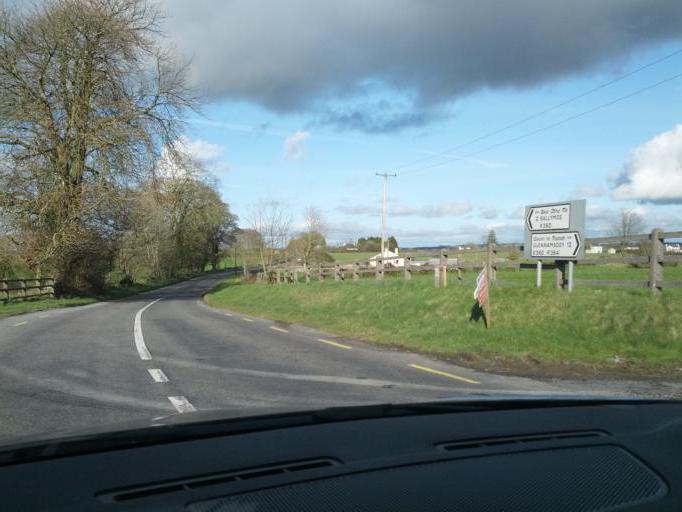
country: IE
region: Connaught
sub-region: Roscommon
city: Castlerea
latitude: 53.6862
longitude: -8.4819
